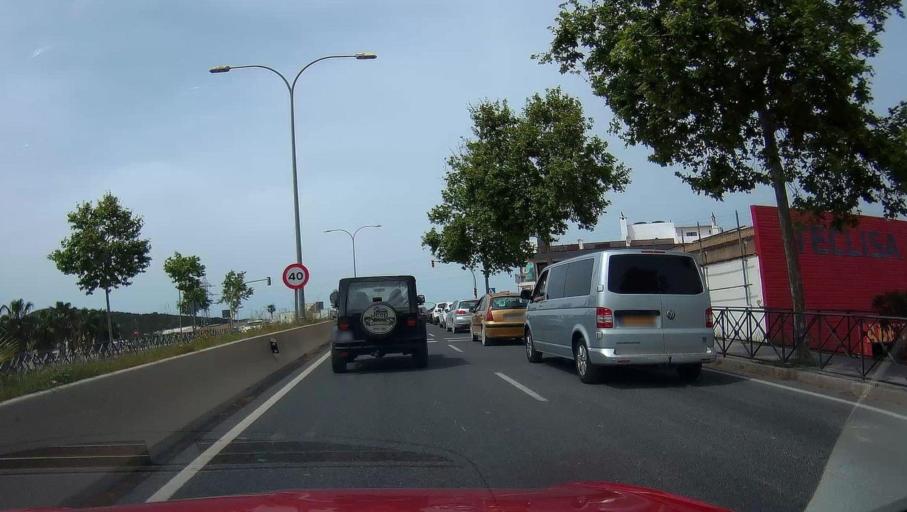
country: ES
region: Balearic Islands
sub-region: Illes Balears
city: Ibiza
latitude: 38.9193
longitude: 1.4262
